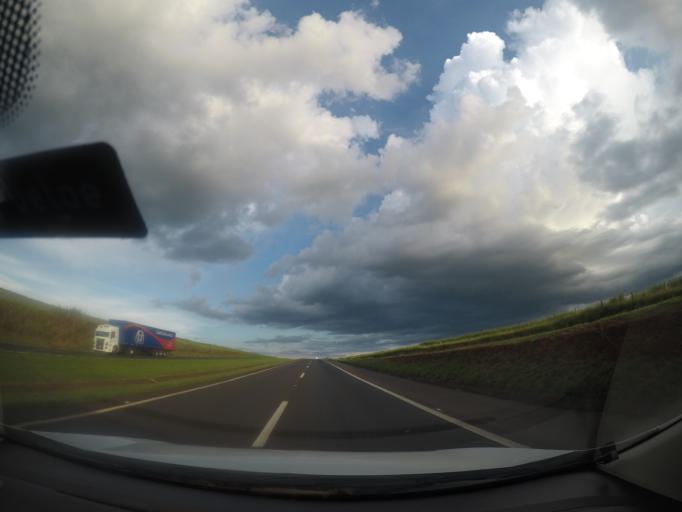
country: BR
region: Sao Paulo
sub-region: Ibate
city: Ibate
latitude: -21.8900
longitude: -48.0768
